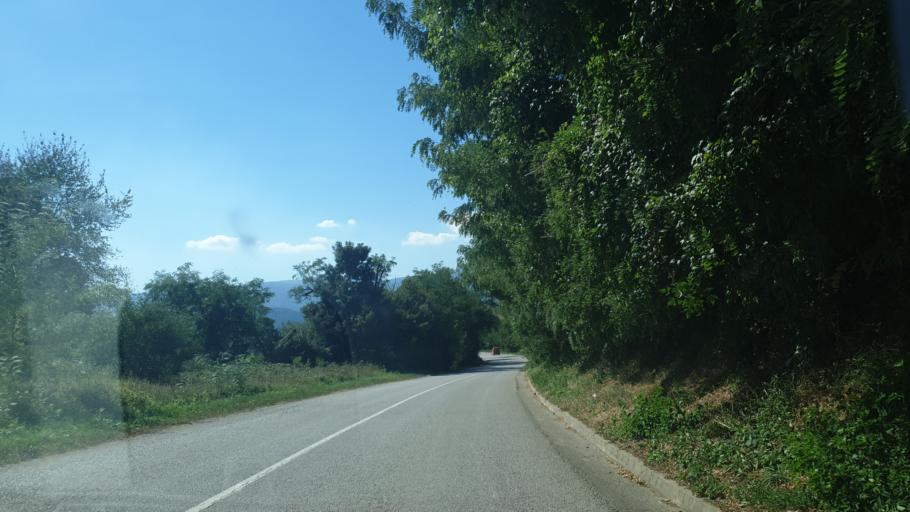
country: RS
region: Central Serbia
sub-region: Kolubarski Okrug
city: Mionica
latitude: 44.1969
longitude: 20.0783
